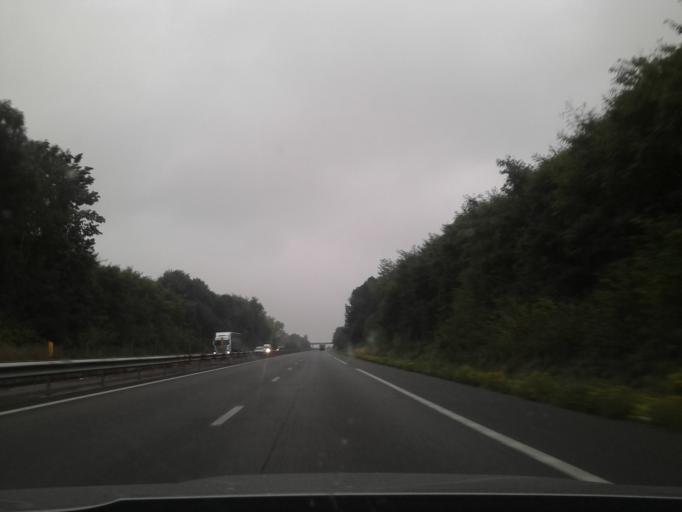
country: FR
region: Nord-Pas-de-Calais
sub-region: Departement du Nord
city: Neuville-Saint-Remy
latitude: 50.2087
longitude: 3.2286
